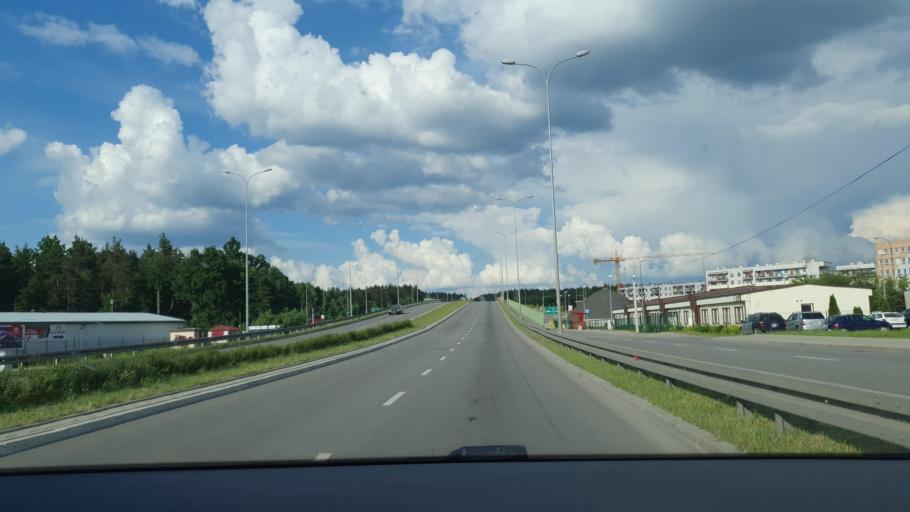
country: PL
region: Podlasie
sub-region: Bialystok
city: Bialystok
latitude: 53.1262
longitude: 23.2150
